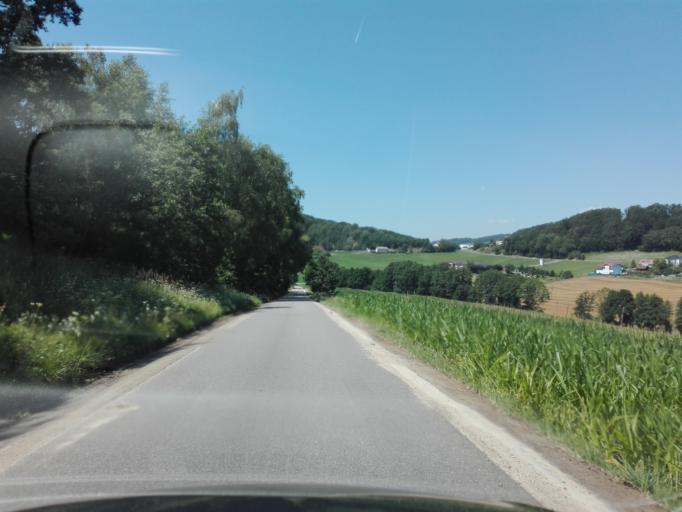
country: AT
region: Upper Austria
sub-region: Politischer Bezirk Urfahr-Umgebung
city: Gallneukirchen
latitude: 48.3269
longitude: 14.3967
